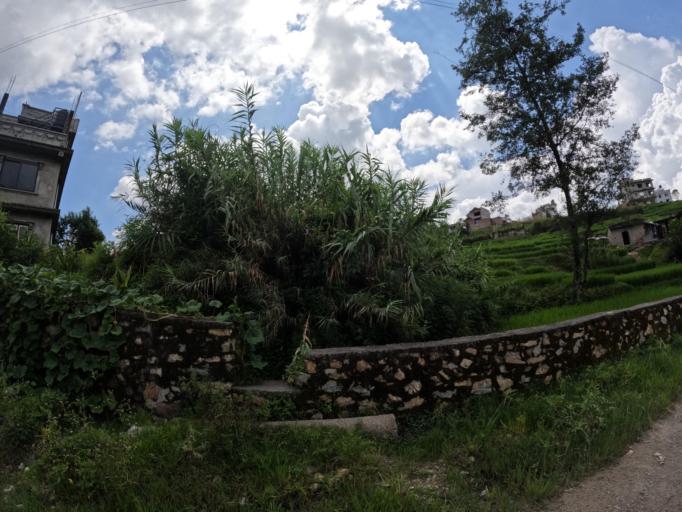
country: NP
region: Central Region
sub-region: Bagmati Zone
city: Kathmandu
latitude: 27.7780
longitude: 85.3286
